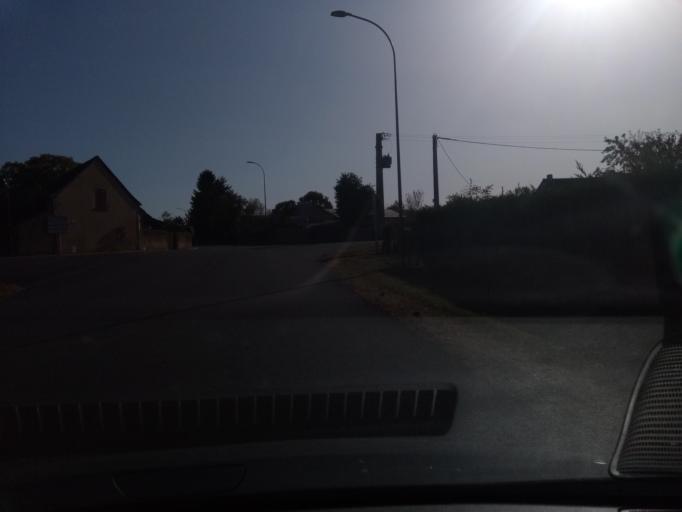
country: FR
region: Centre
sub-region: Departement de l'Indre
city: Belabre
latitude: 46.4663
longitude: 1.0370
